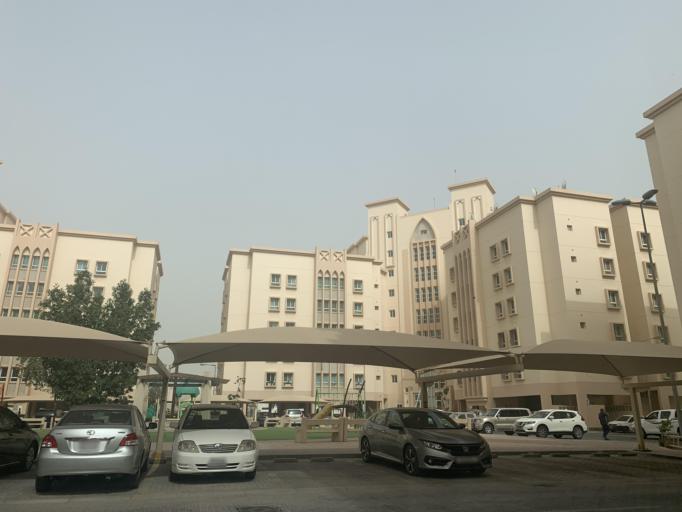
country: BH
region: Manama
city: Jidd Hafs
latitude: 26.2235
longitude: 50.5527
